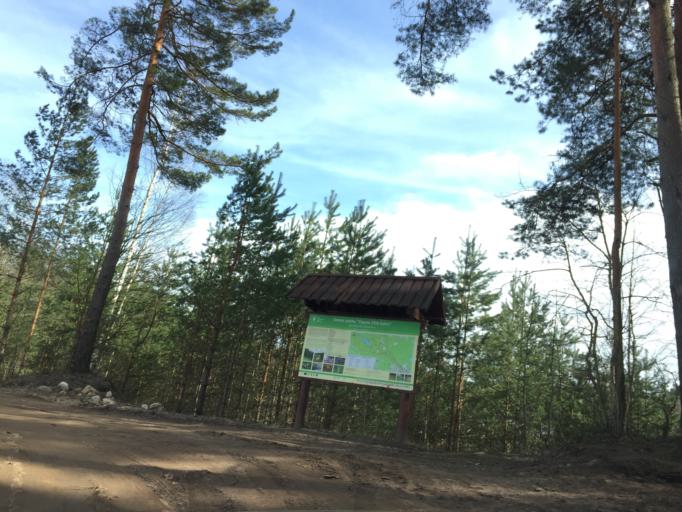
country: LV
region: Ikskile
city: Ikskile
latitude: 56.8431
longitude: 24.5437
